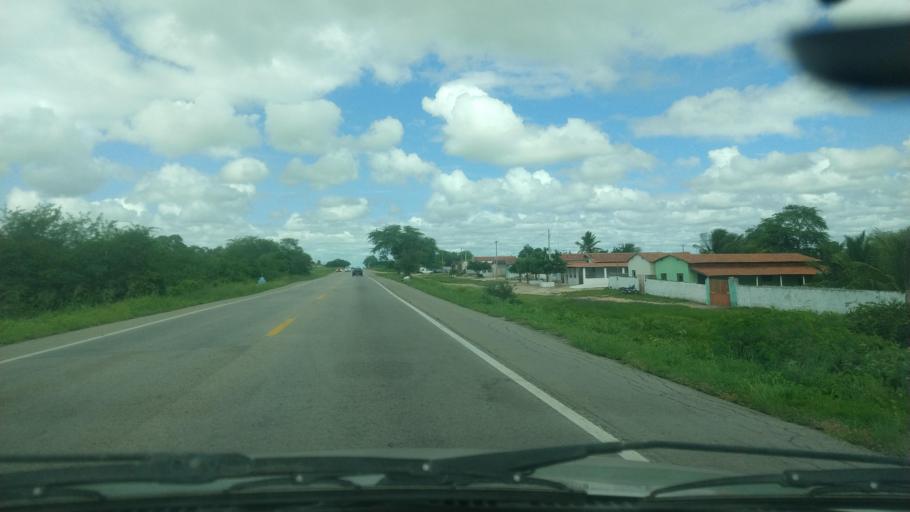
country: BR
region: Rio Grande do Norte
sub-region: Tangara
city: Tangara
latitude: -6.1684
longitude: -35.7601
